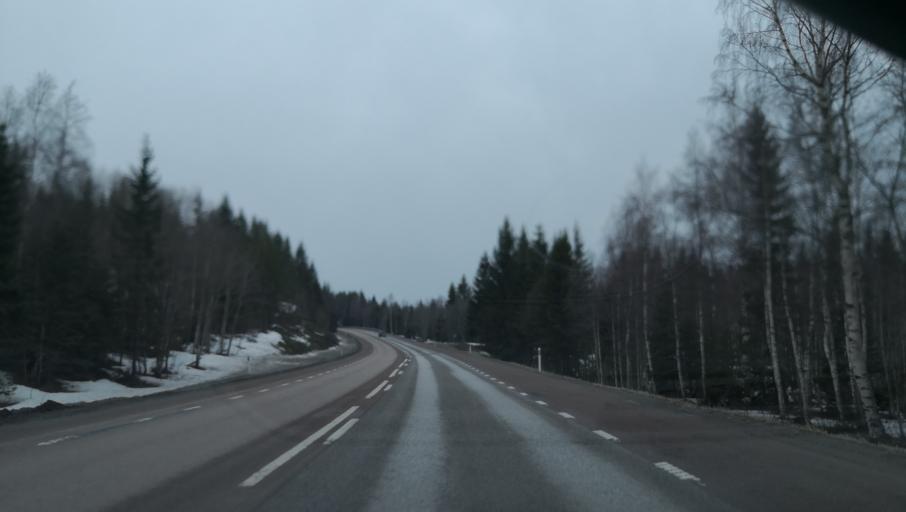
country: SE
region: Vaesternorrland
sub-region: Haernoesands Kommun
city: Haernoesand
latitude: 62.7038
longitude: 17.8605
